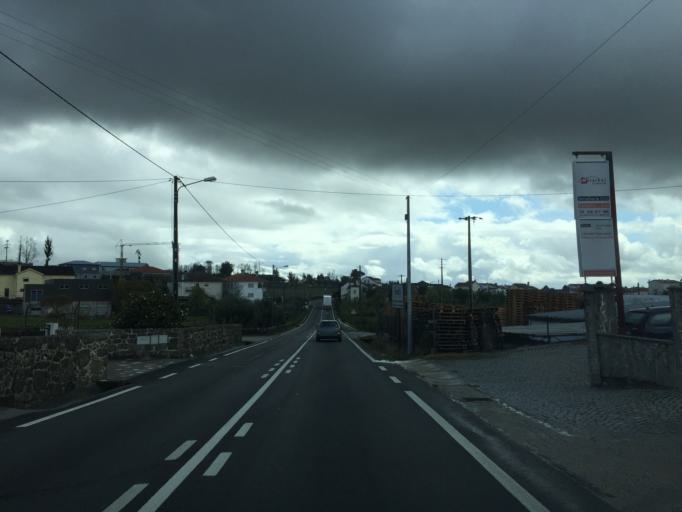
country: PT
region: Coimbra
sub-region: Oliveira do Hospital
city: Oliveira do Hospital
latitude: 40.3165
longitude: -7.8900
